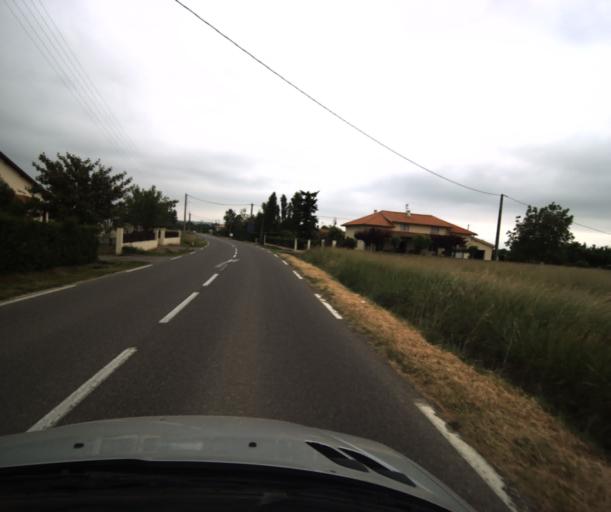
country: FR
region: Midi-Pyrenees
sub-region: Departement du Tarn-et-Garonne
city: Saint-Nicolas-de-la-Grave
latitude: 44.0554
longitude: 1.0260
